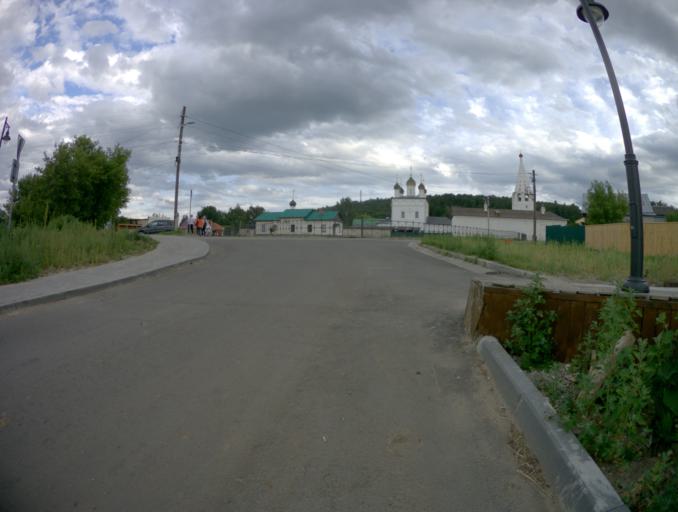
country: RU
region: Vladimir
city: Gorokhovets
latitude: 56.2080
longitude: 42.6797
